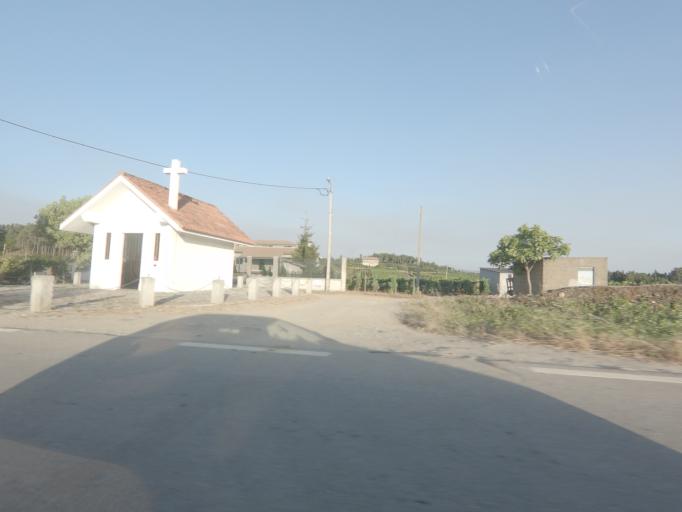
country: PT
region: Vila Real
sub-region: Sabrosa
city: Vilela
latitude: 41.2013
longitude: -7.6831
